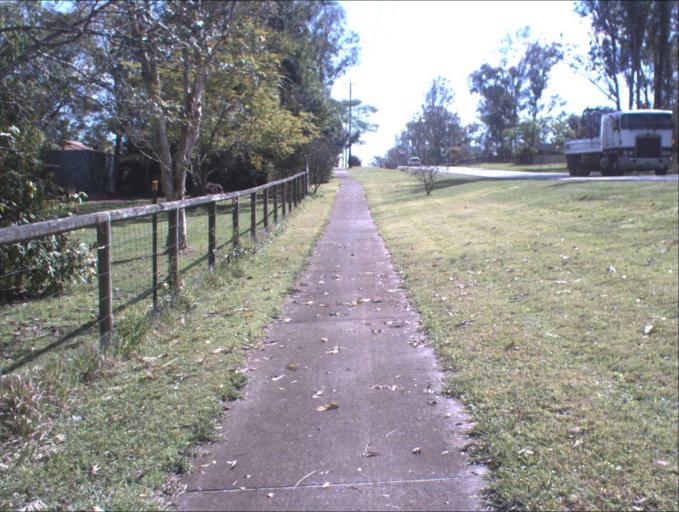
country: AU
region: Queensland
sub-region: Logan
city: Park Ridge South
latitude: -27.7164
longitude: 152.9766
